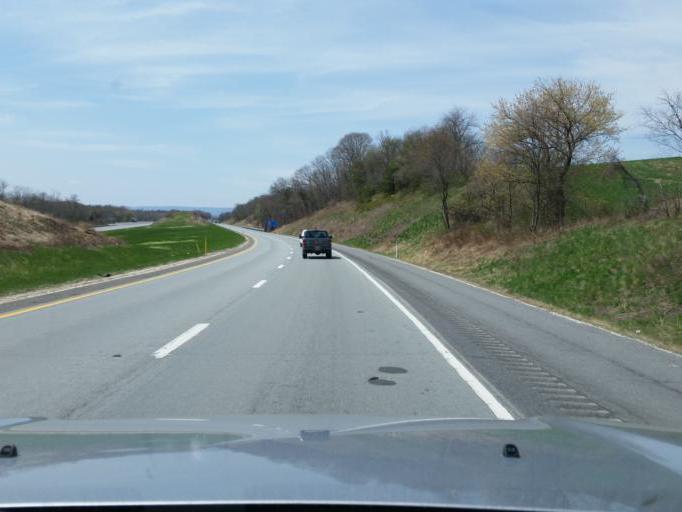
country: US
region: Pennsylvania
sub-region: Perry County
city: Newport
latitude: 40.4943
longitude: -77.0846
